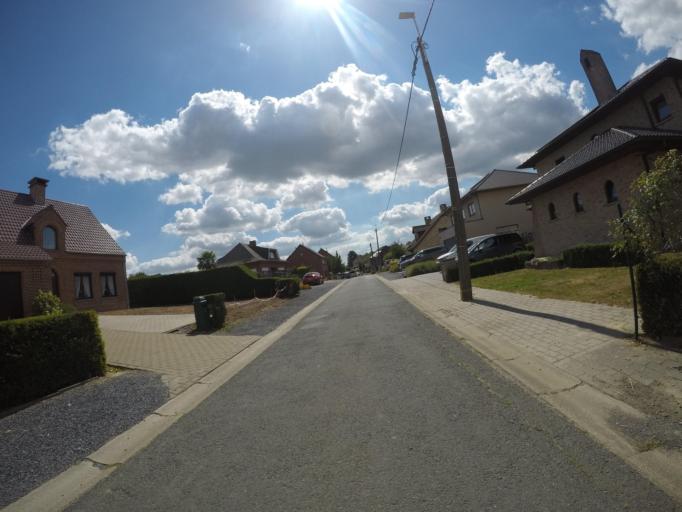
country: BE
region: Flanders
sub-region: Provincie Vlaams-Brabant
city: Ternat
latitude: 50.8461
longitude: 4.1390
